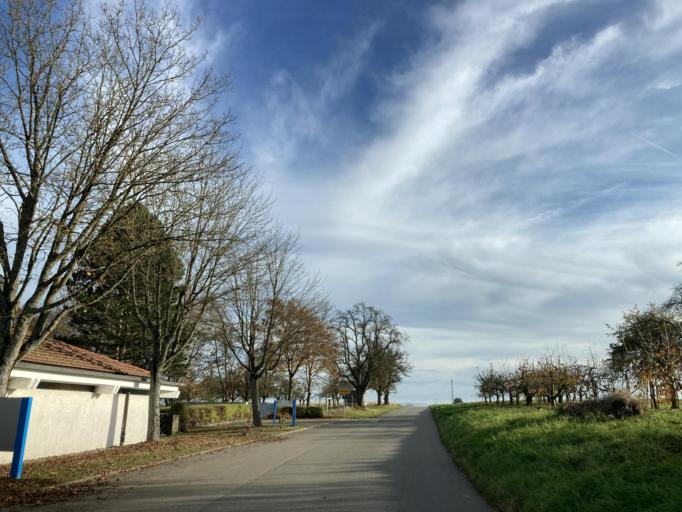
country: DE
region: Baden-Wuerttemberg
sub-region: Regierungsbezirk Stuttgart
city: Bondorf
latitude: 48.4708
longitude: 8.8218
